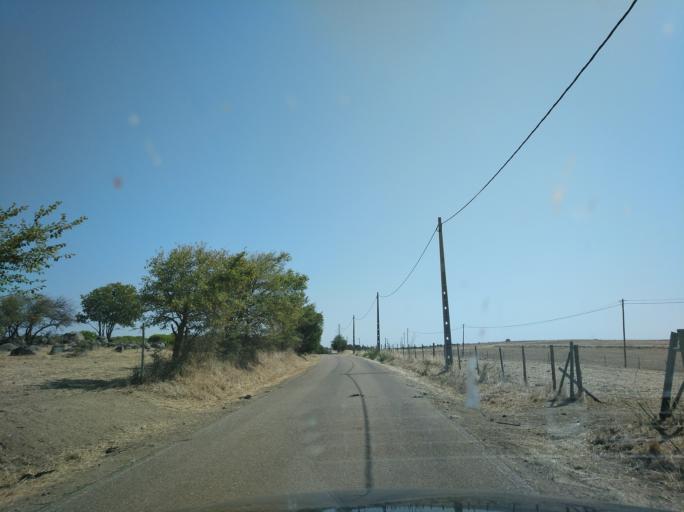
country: PT
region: Portalegre
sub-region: Campo Maior
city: Campo Maior
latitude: 39.0236
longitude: -7.0439
